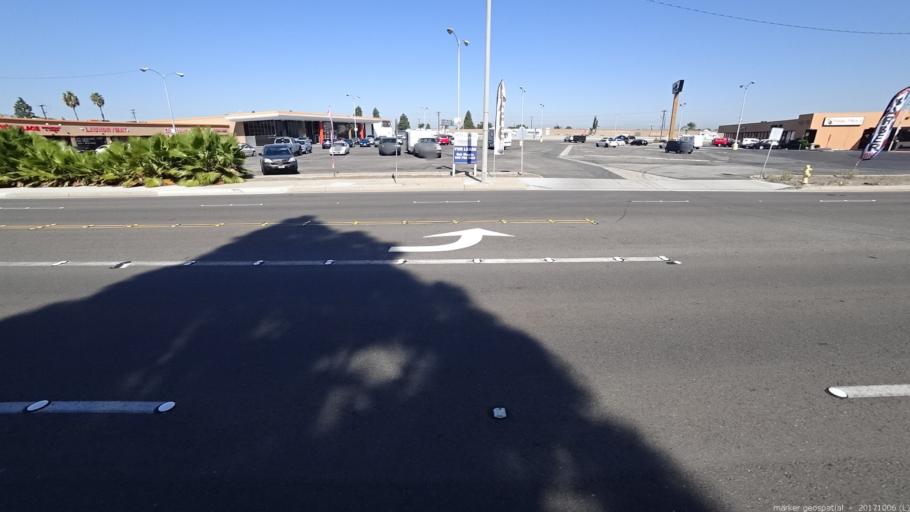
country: US
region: California
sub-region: Orange County
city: Westminster
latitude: 33.7726
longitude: -118.0225
